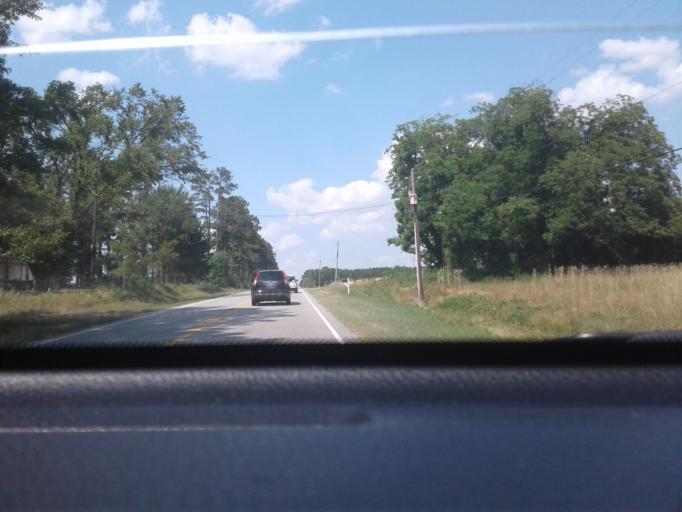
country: US
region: North Carolina
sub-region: Harnett County
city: Erwin
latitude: 35.2046
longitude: -78.6868
